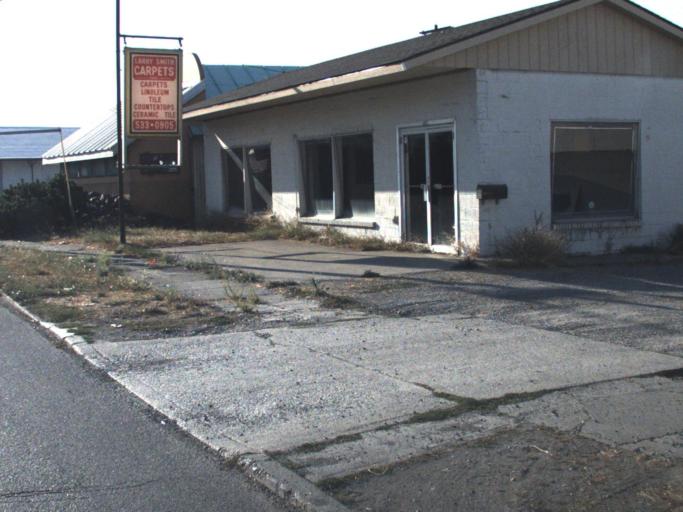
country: US
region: Washington
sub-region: Spokane County
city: Millwood
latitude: 47.6709
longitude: -117.3527
